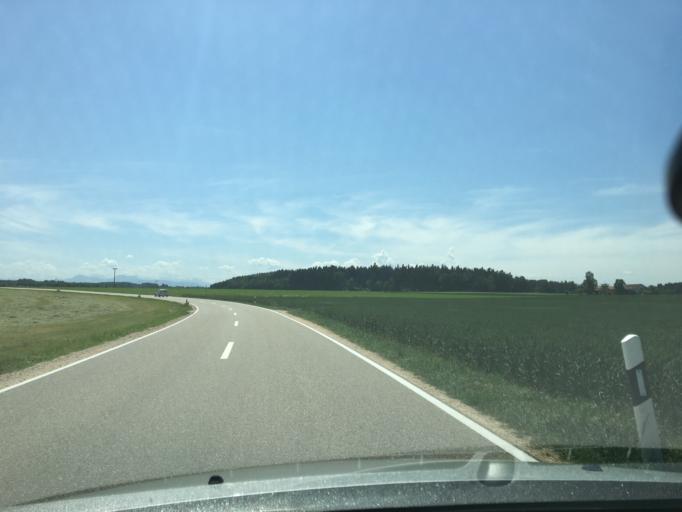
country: DE
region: Bavaria
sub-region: Upper Bavaria
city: Halsbach
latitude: 48.1044
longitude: 12.6828
